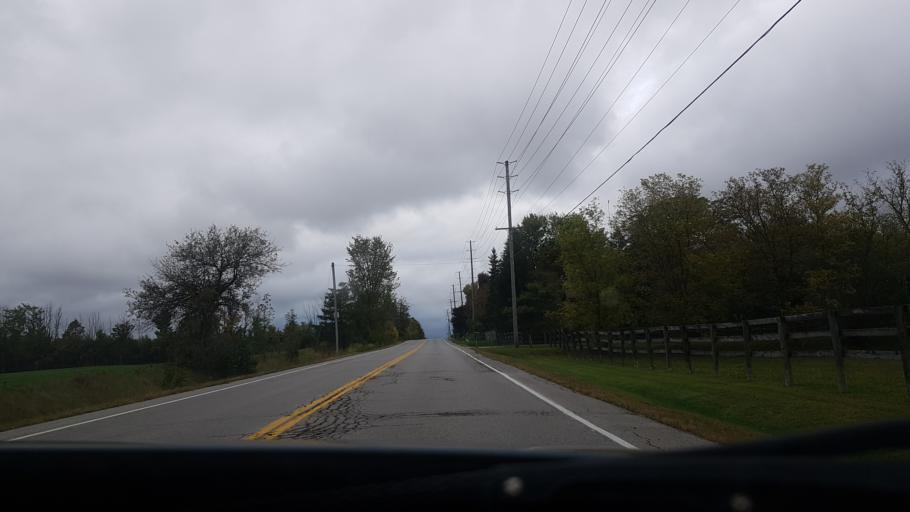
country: CA
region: Ontario
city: Newmarket
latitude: 44.0567
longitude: -79.3861
